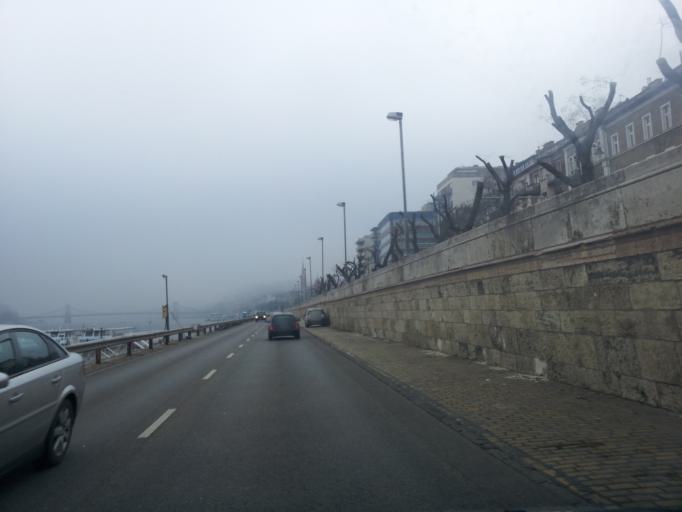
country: HU
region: Budapest
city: Budapest II. keruelet
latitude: 47.5101
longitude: 19.0396
